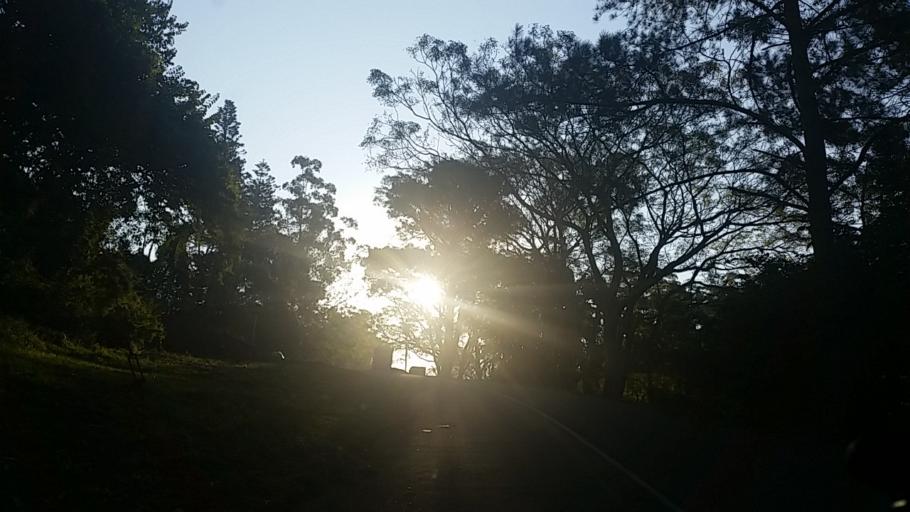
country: ZA
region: KwaZulu-Natal
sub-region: eThekwini Metropolitan Municipality
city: Berea
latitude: -29.8424
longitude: 30.9179
